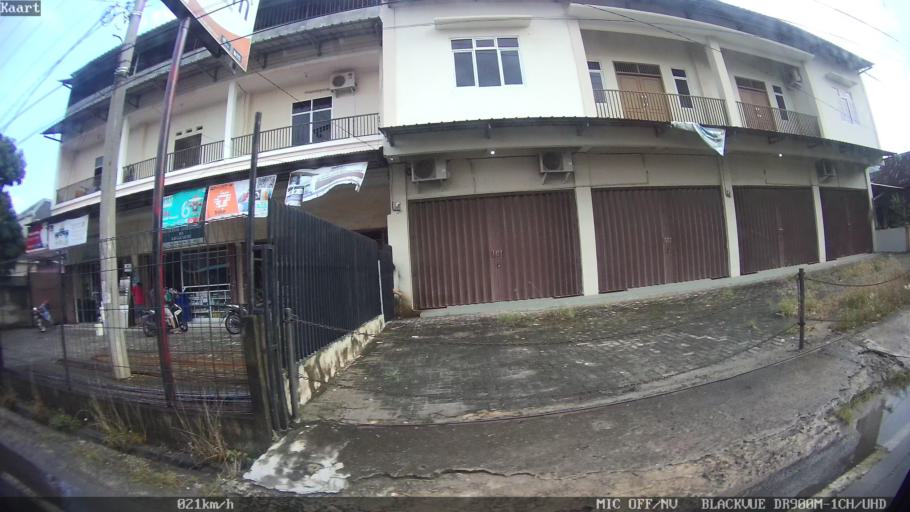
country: ID
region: Lampung
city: Kedaton
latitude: -5.3910
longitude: 105.3032
